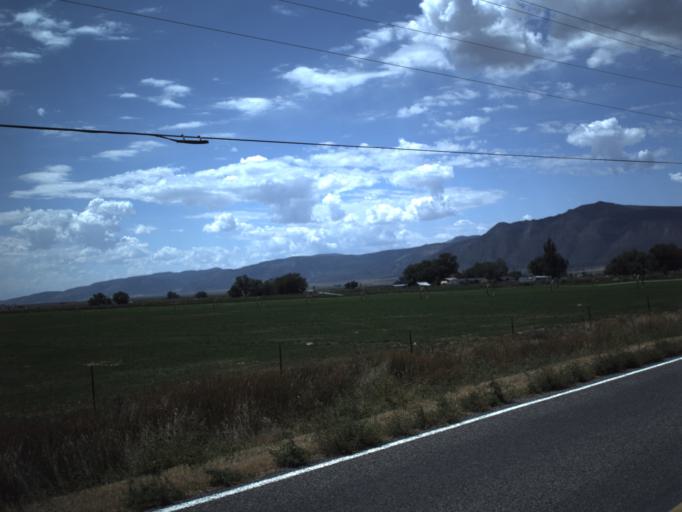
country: US
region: Utah
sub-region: Sanpete County
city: Moroni
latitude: 39.4762
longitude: -111.5560
